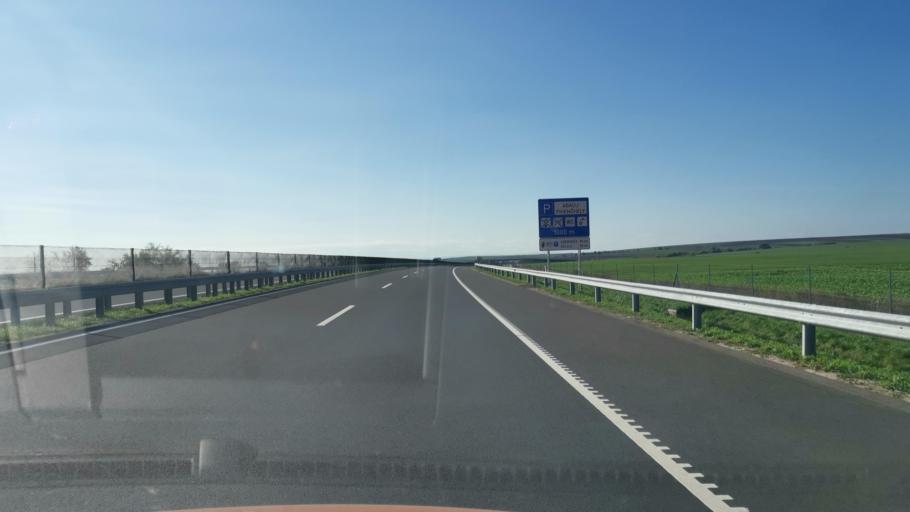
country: HU
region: Borsod-Abauj-Zemplen
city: Halmaj
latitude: 48.3002
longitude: 21.0535
